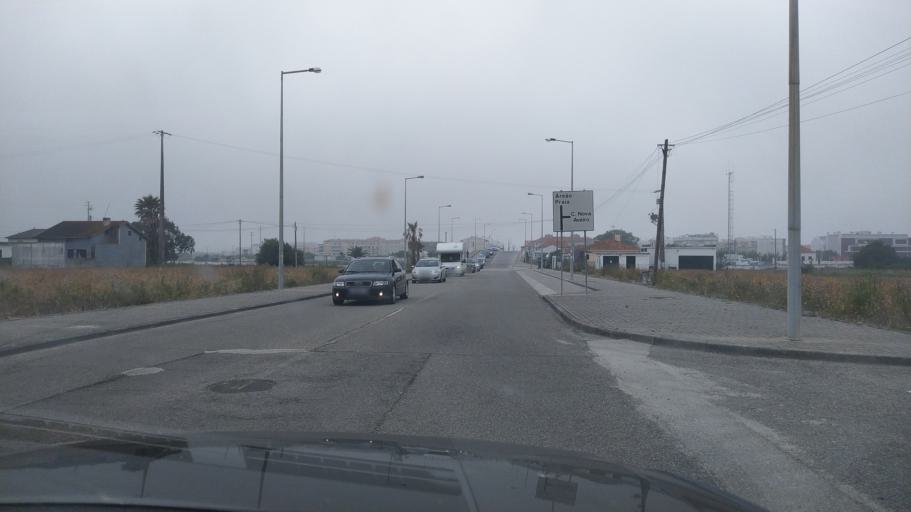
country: PT
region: Aveiro
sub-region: Ilhavo
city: Gafanha da Encarnacao
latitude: 40.5599
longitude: -8.7556
